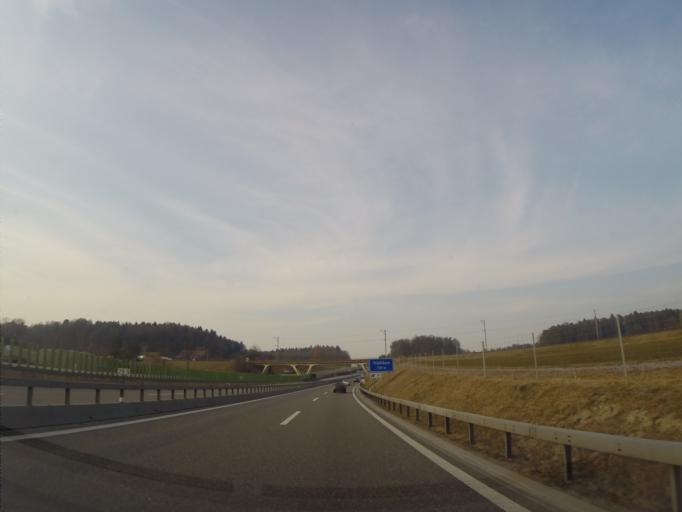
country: CH
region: Zurich
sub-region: Bezirk Andelfingen
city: Kleinandelfingen
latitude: 47.6074
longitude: 8.6870
